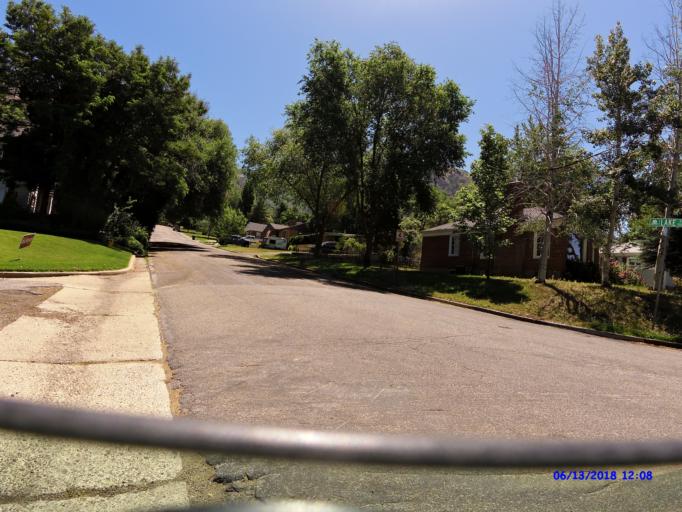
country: US
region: Utah
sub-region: Weber County
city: Ogden
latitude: 41.2192
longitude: -111.9345
